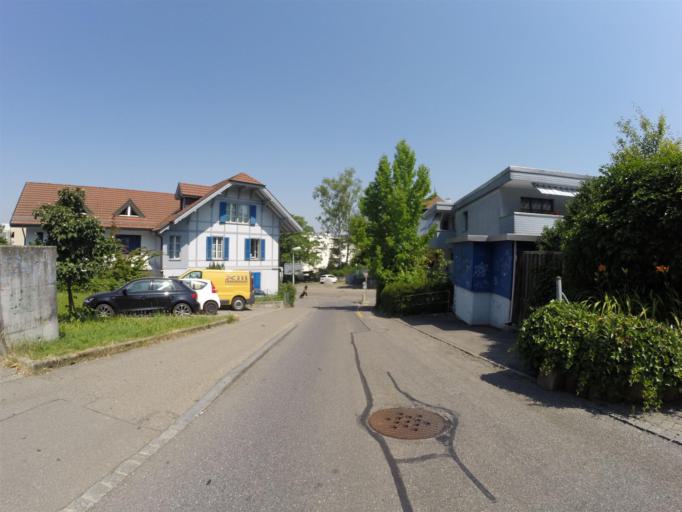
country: CH
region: Bern
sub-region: Bern-Mittelland District
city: Bolligen
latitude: 46.9572
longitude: 7.4942
